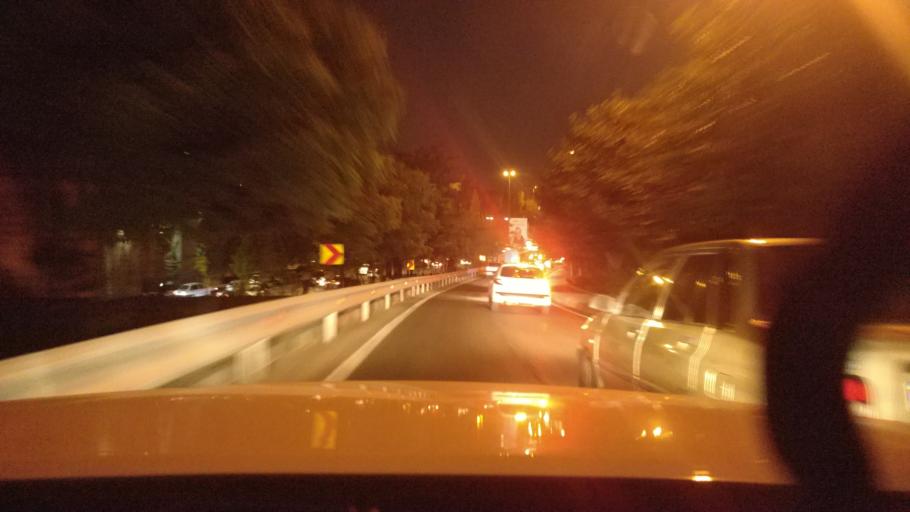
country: IR
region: Tehran
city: Tehran
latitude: 35.7464
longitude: 51.4016
